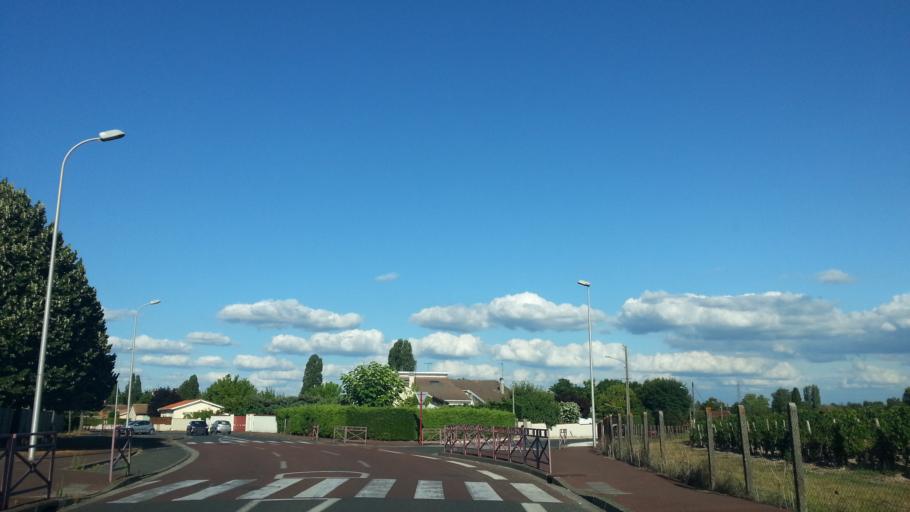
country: FR
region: Aquitaine
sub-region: Departement de la Gironde
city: Villenave-d'Ornon
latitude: 44.7596
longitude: -0.5645
